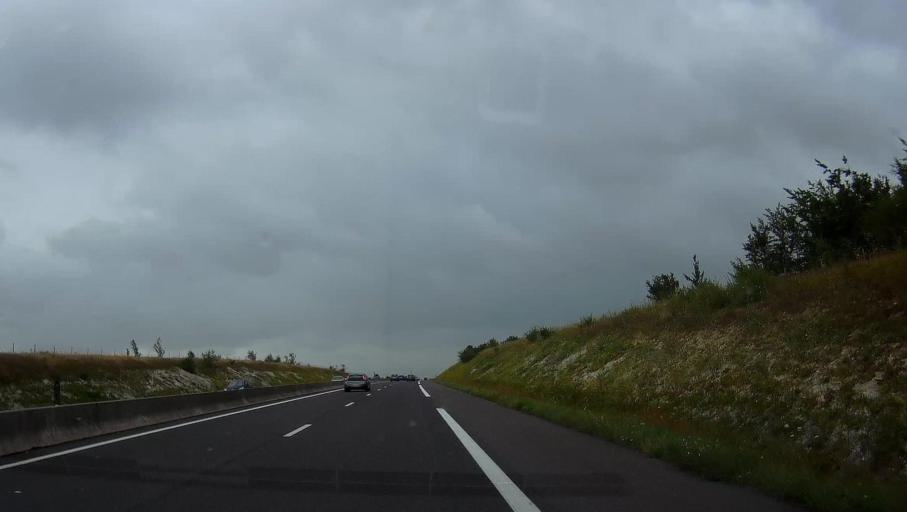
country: FR
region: Champagne-Ardenne
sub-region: Departement de l'Aube
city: Mailly-le-Camp
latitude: 48.6562
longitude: 4.1741
